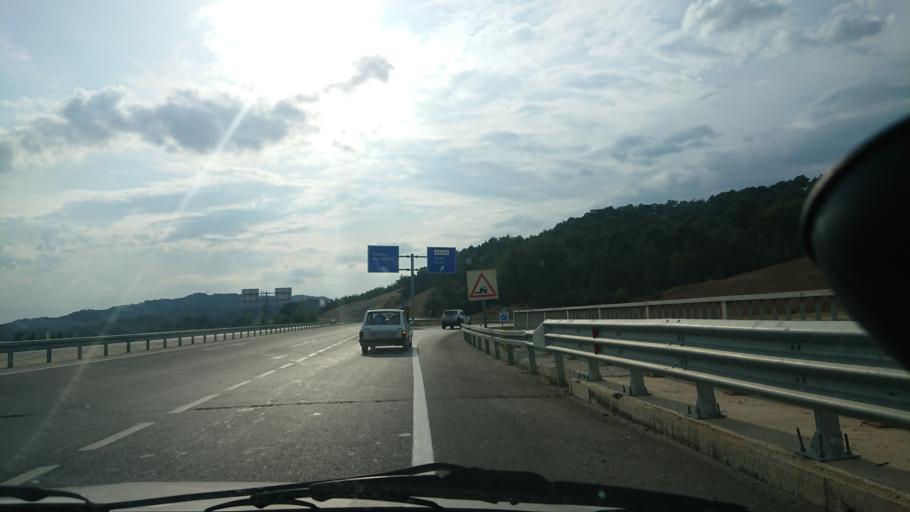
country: TR
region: Kuetahya
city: Gediz
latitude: 38.9354
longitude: 29.3109
